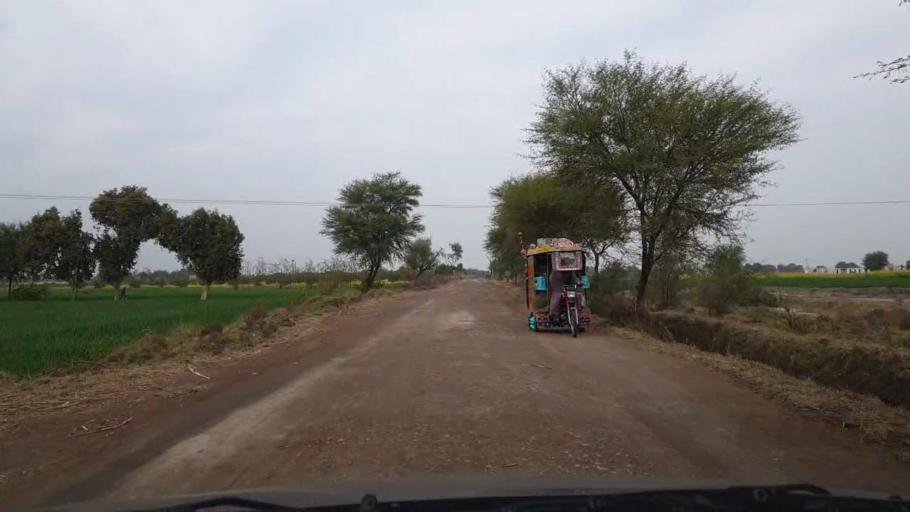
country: PK
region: Sindh
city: Sanghar
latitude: 26.1000
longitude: 68.8963
